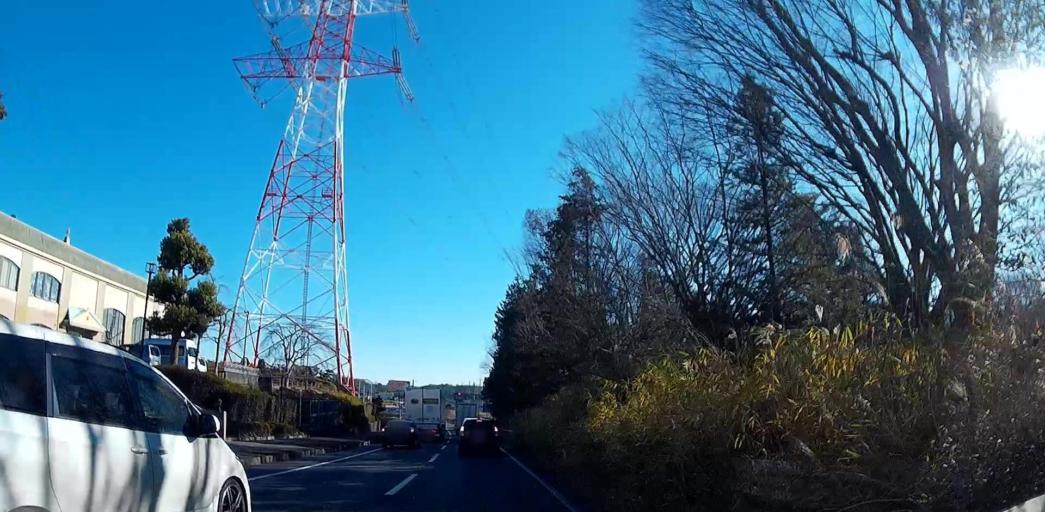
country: JP
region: Chiba
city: Shiroi
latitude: 35.7877
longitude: 140.0796
